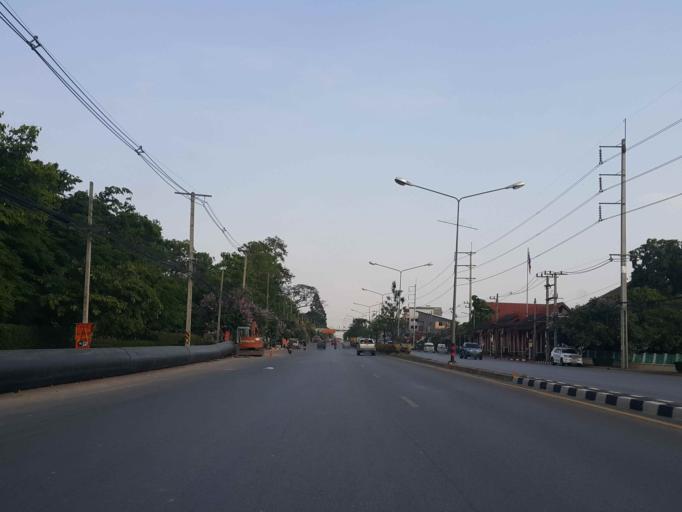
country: TH
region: Chiang Mai
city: San Sai
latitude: 18.9045
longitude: 99.0041
